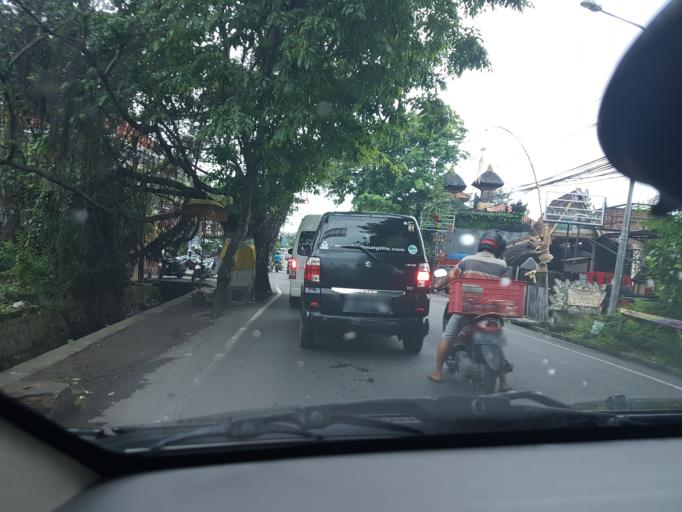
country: ID
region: Bali
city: Kuta
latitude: -8.6715
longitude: 115.1648
